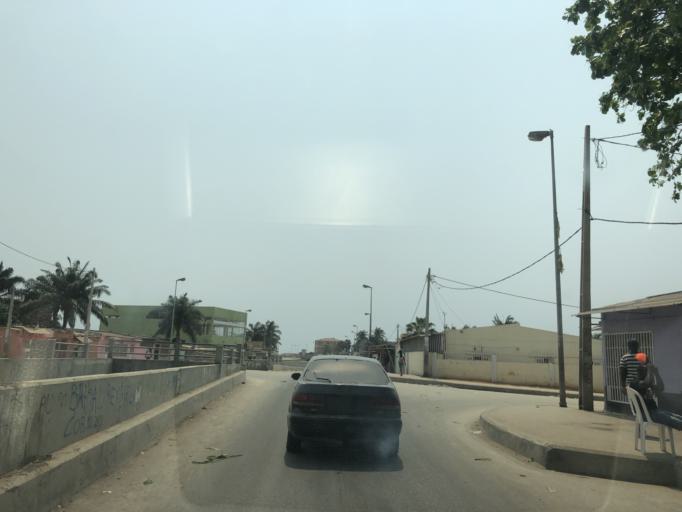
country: AO
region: Luanda
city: Luanda
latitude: -8.8494
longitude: 13.2092
